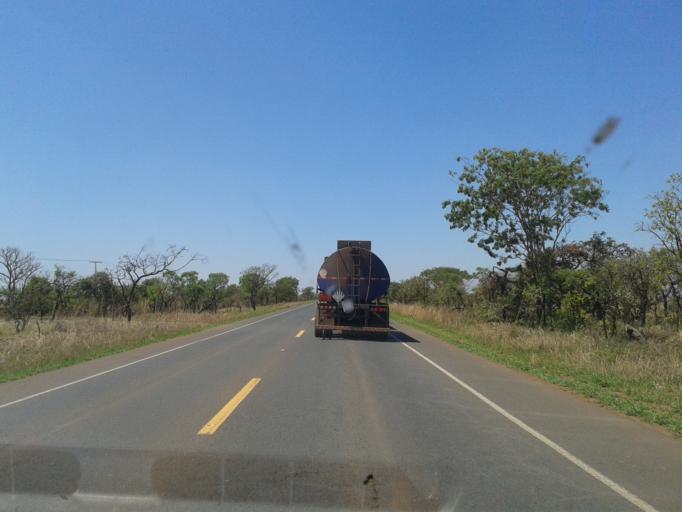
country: BR
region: Minas Gerais
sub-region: Araxa
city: Araxa
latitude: -19.3031
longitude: -47.3955
